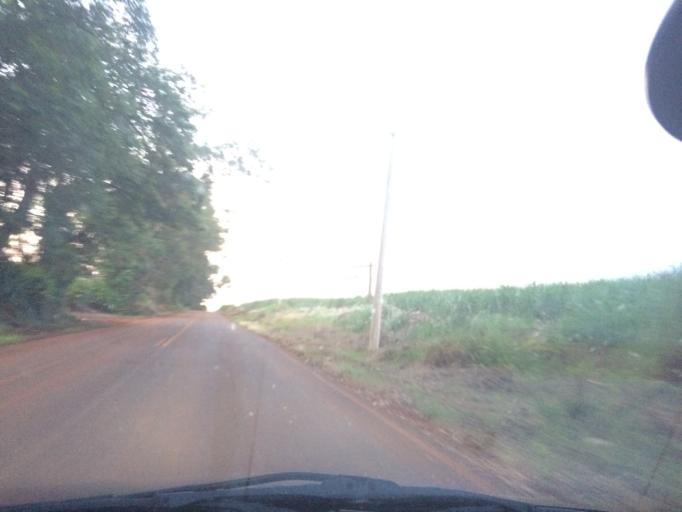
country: BR
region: Sao Paulo
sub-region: Tambau
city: Tambau
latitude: -21.7063
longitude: -47.2025
